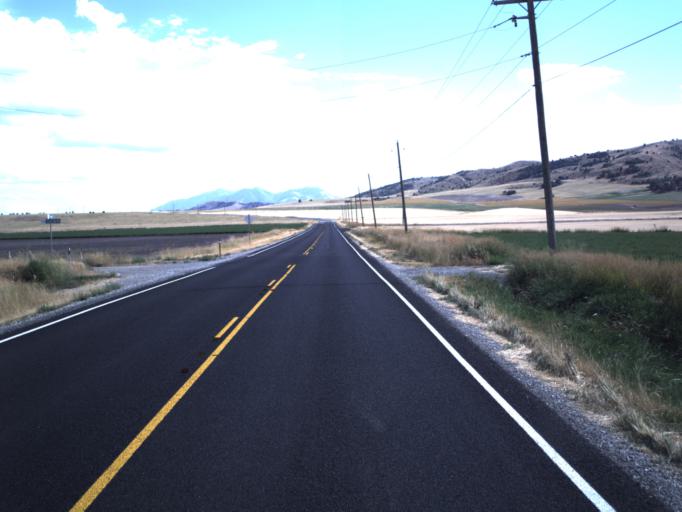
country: US
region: Utah
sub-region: Cache County
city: Benson
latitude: 41.9049
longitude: -112.0457
